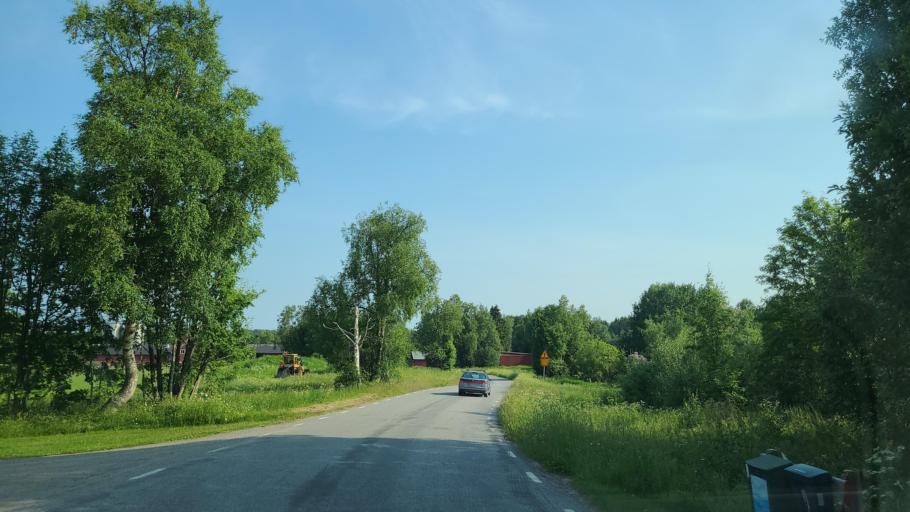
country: SE
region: Vaesterbotten
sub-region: Skelleftea Kommun
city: Burea
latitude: 64.3494
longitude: 21.3367
